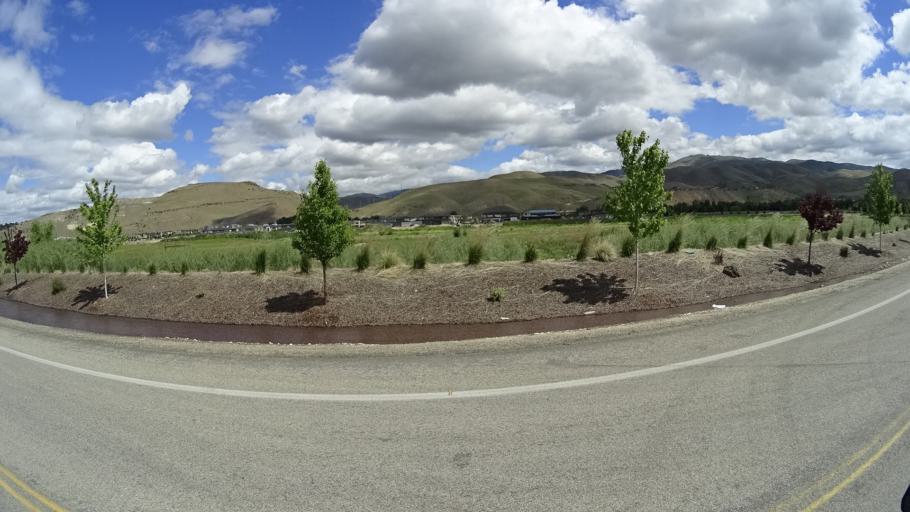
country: US
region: Idaho
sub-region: Ada County
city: Boise
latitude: 43.5692
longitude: -116.1304
